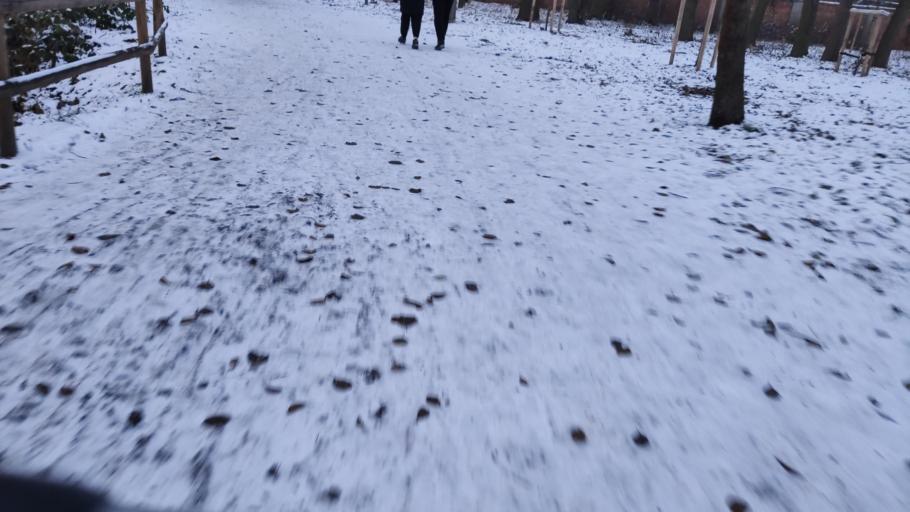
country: PL
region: Lower Silesian Voivodeship
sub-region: Powiat wroclawski
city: Wroclaw
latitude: 51.0858
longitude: 16.9916
